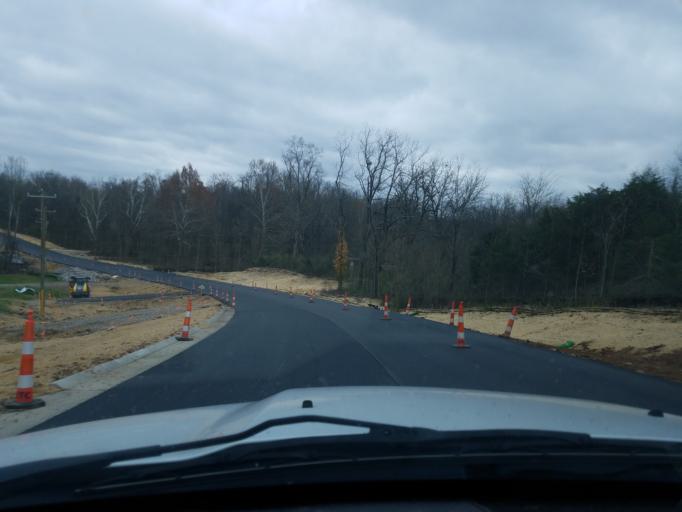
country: US
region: Indiana
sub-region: Clark County
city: Oak Park
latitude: 38.3447
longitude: -85.6654
